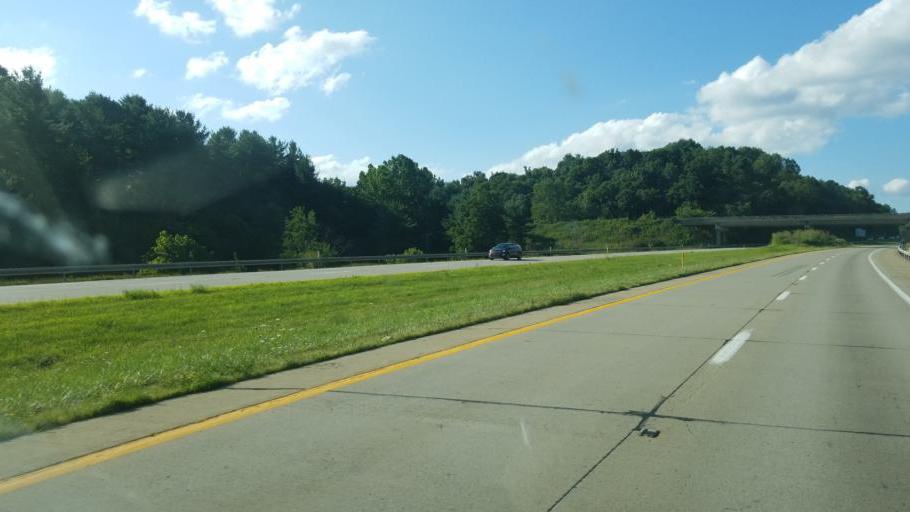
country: US
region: Pennsylvania
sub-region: Greene County
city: Morrisville
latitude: 39.9212
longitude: -80.1634
